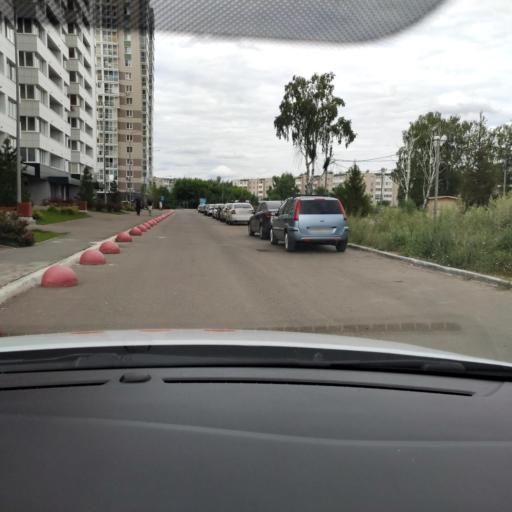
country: RU
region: Tatarstan
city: Osinovo
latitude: 55.8446
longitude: 48.9074
